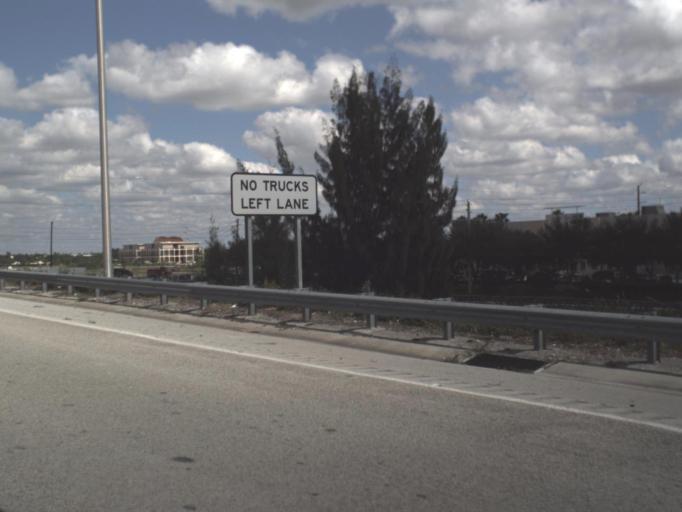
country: US
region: Florida
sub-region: Miami-Dade County
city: Sweetwater
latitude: 25.7951
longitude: -80.3858
